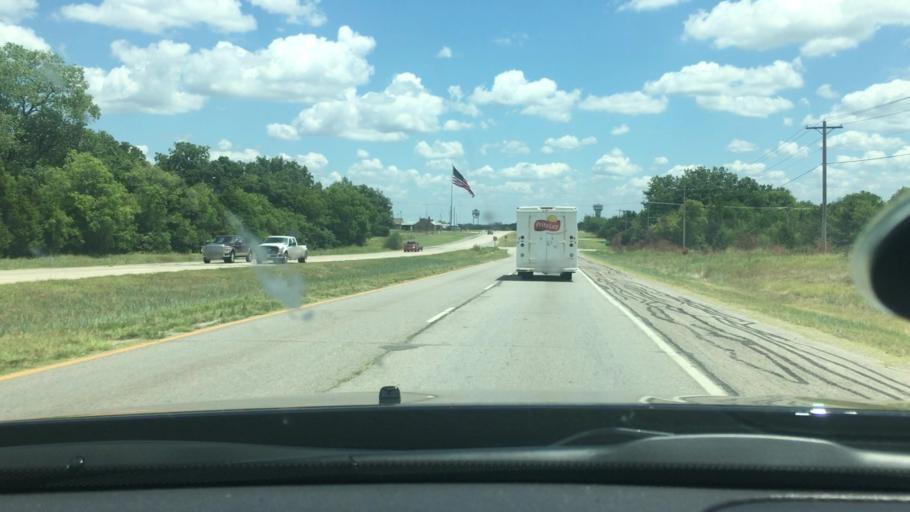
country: US
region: Oklahoma
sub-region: Carter County
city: Lone Grove
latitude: 34.1728
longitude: -97.2150
